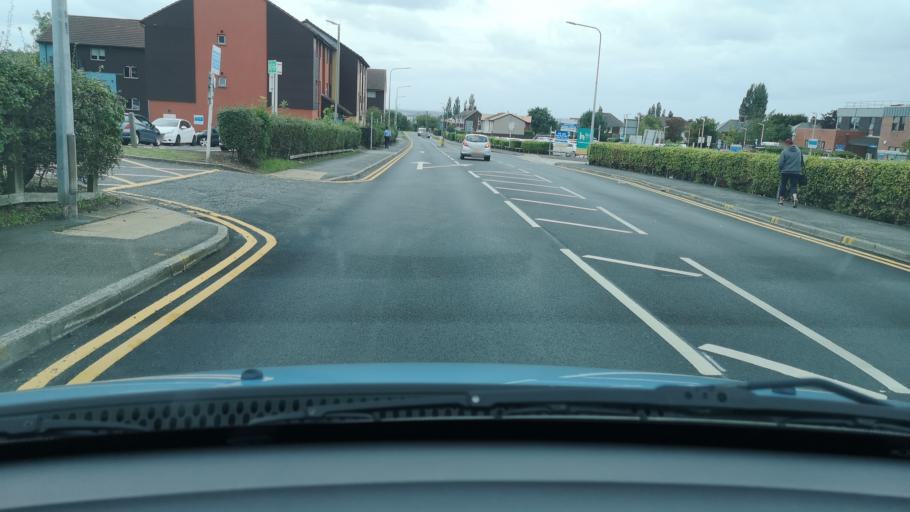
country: GB
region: England
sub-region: North Lincolnshire
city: Scunthorpe
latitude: 53.5860
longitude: -0.6671
